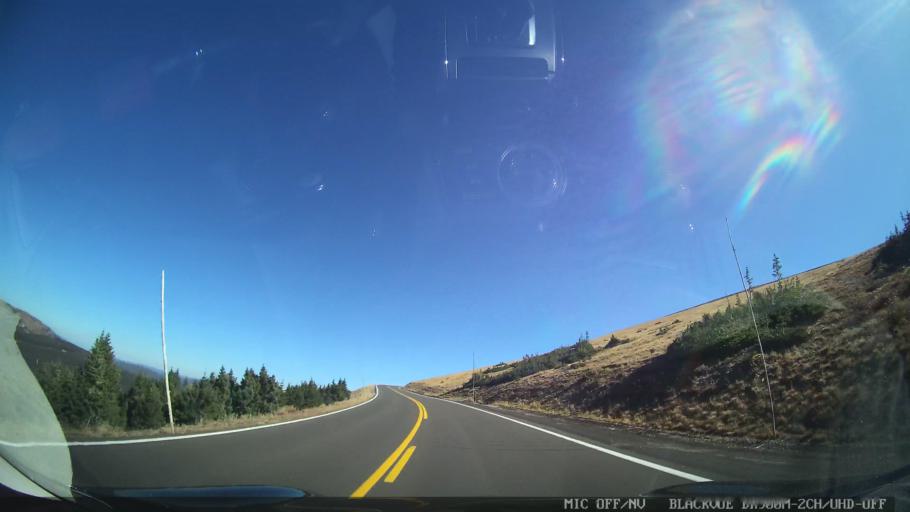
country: US
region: Colorado
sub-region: Larimer County
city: Estes Park
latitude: 40.4426
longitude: -105.7599
